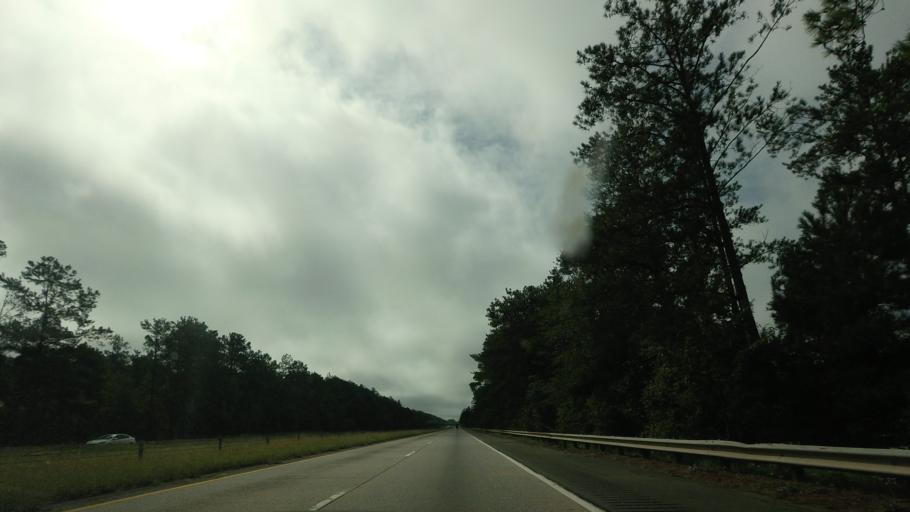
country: US
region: Georgia
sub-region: Bibb County
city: Macon
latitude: 32.7817
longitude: -83.5591
